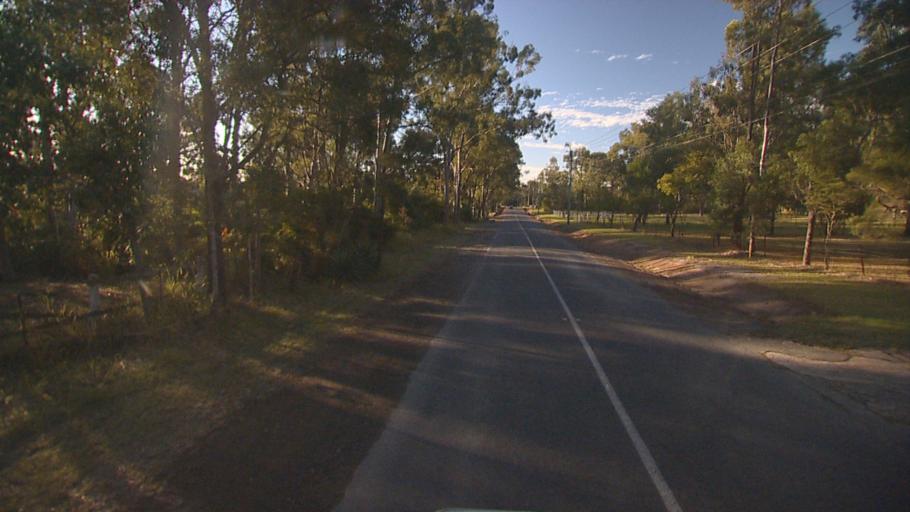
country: AU
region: Queensland
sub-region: Logan
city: Waterford West
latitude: -27.7243
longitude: 153.1475
